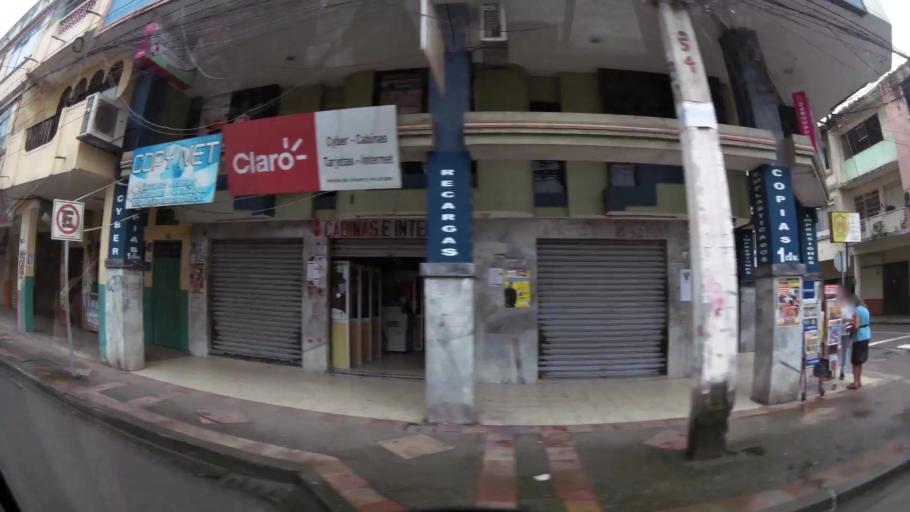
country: EC
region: El Oro
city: Pasaje
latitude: -3.3286
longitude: -79.8080
